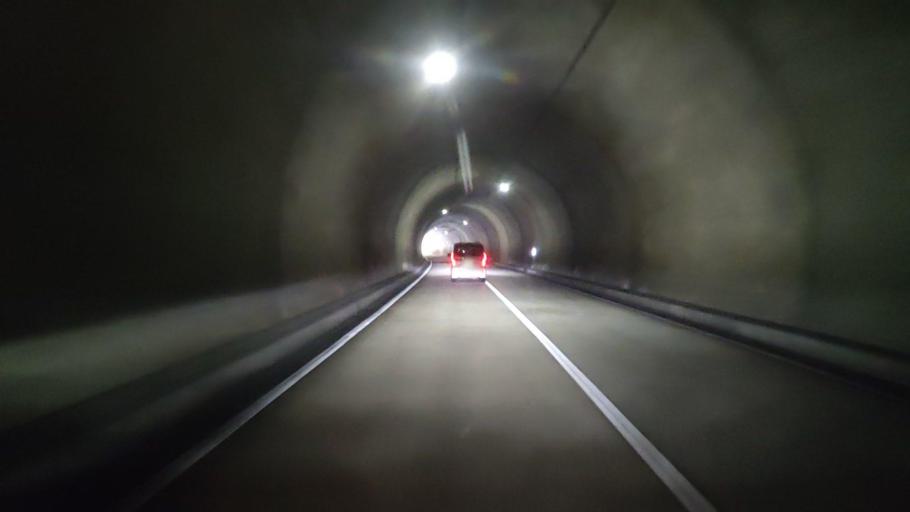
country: JP
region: Wakayama
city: Shingu
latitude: 33.8867
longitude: 135.8794
